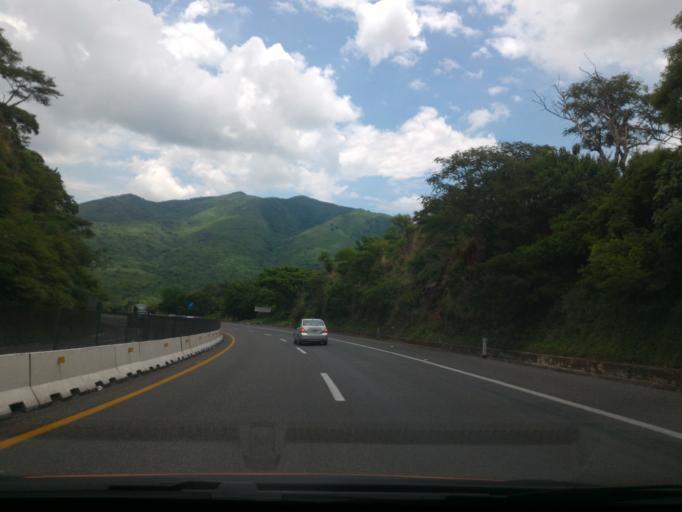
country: MX
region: Jalisco
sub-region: Acatlan de Juarez
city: Villa de los Ninos
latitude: 20.4015
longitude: -103.5581
